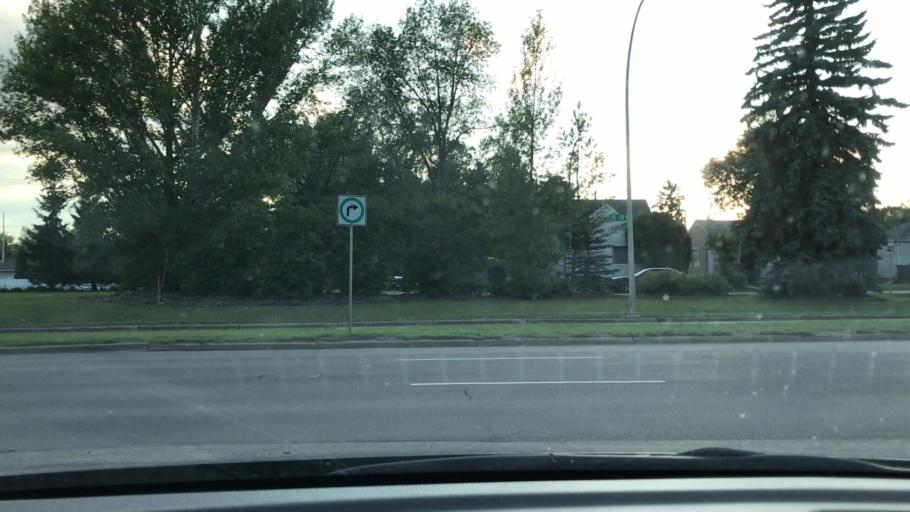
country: CA
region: Alberta
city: Edmonton
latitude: 53.5151
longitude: -113.4427
